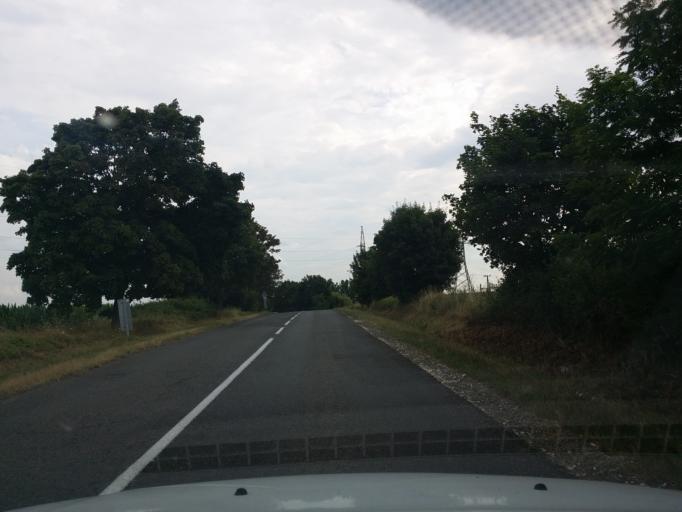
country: HU
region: Nograd
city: Bercel
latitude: 47.8909
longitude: 19.3691
